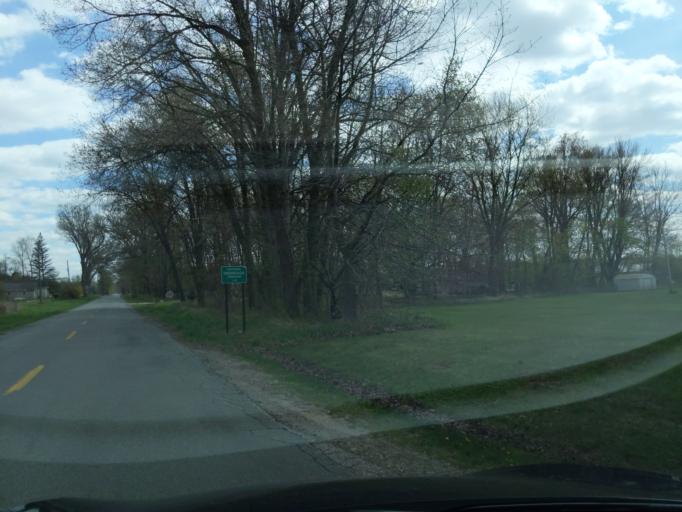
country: US
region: Michigan
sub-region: Eaton County
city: Eaton Rapids
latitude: 42.5093
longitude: -84.5465
